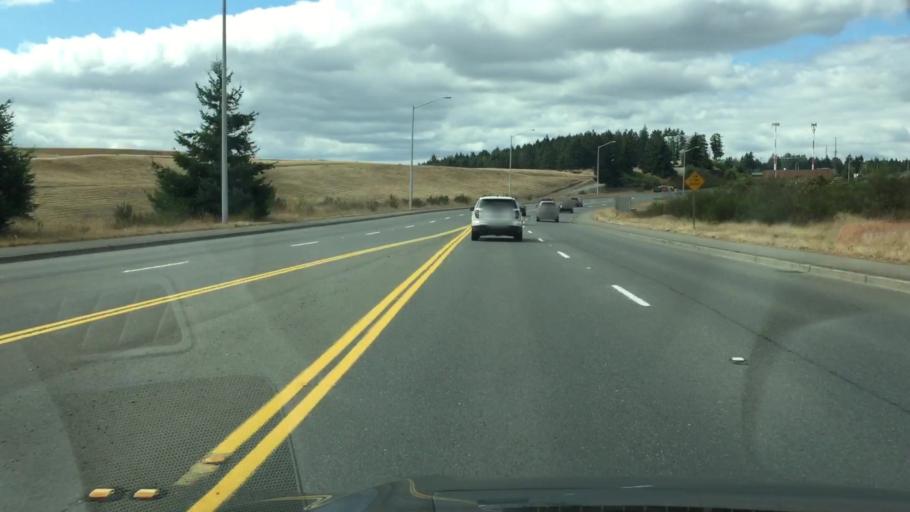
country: US
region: Washington
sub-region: Pierce County
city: Graham
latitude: 47.0975
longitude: -122.2854
